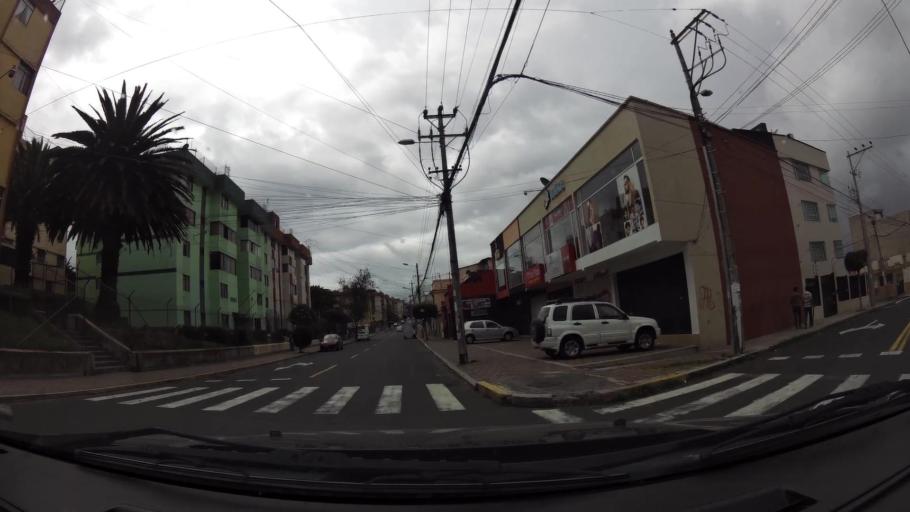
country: EC
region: Pichincha
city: Quito
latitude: -0.1280
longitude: -78.5018
